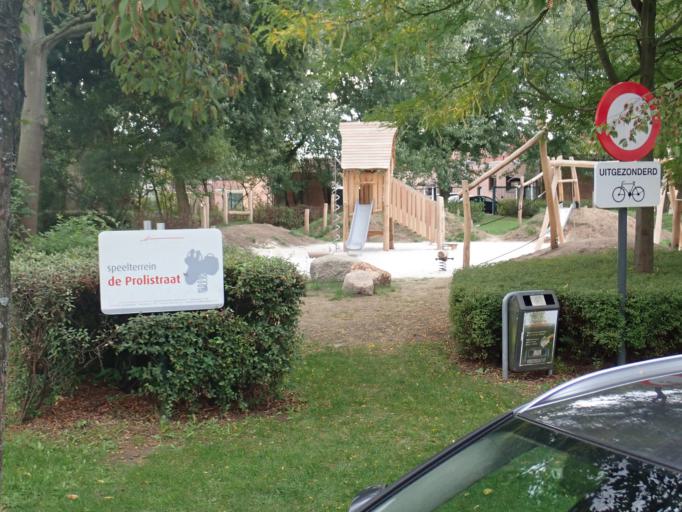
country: BE
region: Flanders
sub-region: Provincie Antwerpen
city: Brasschaat
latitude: 51.3186
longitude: 4.5046
